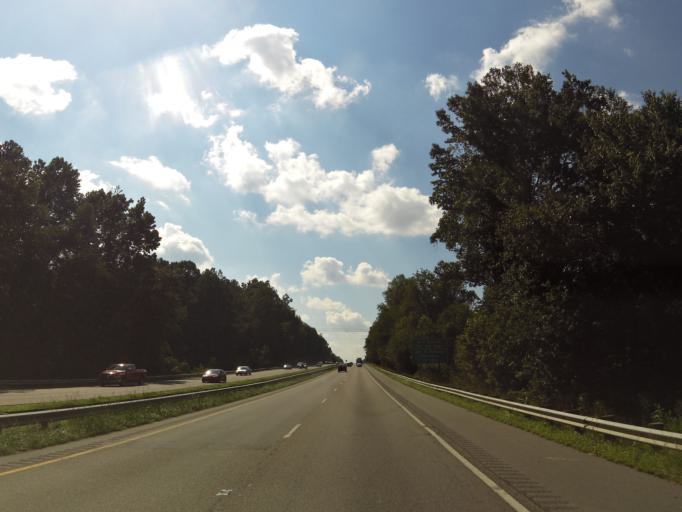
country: US
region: North Carolina
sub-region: Burke County
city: Salem
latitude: 35.7183
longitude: -81.6833
